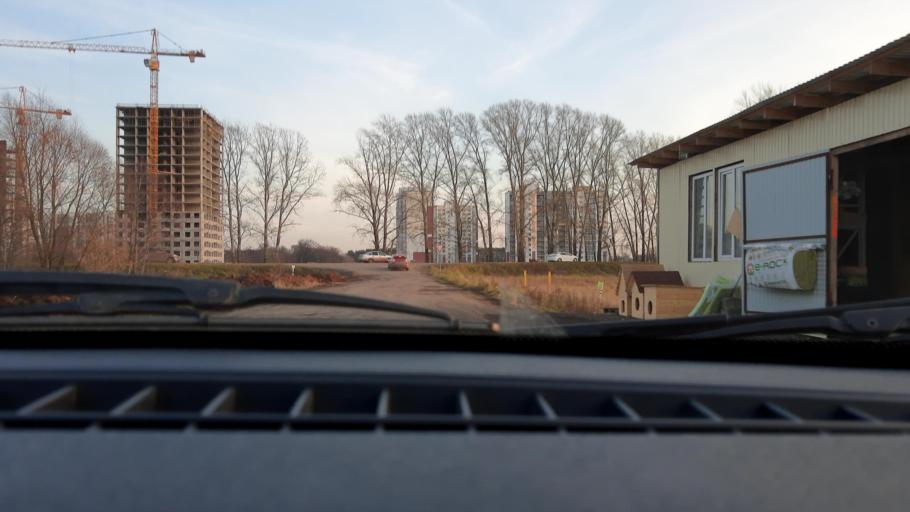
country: RU
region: Bashkortostan
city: Mikhaylovka
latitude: 54.7941
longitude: 55.8414
